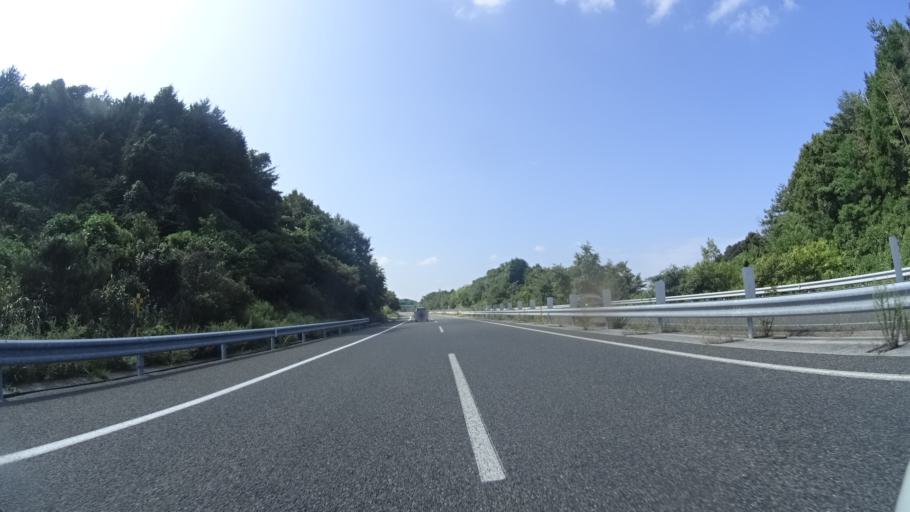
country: JP
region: Shimane
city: Hamada
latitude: 34.9121
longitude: 132.1235
